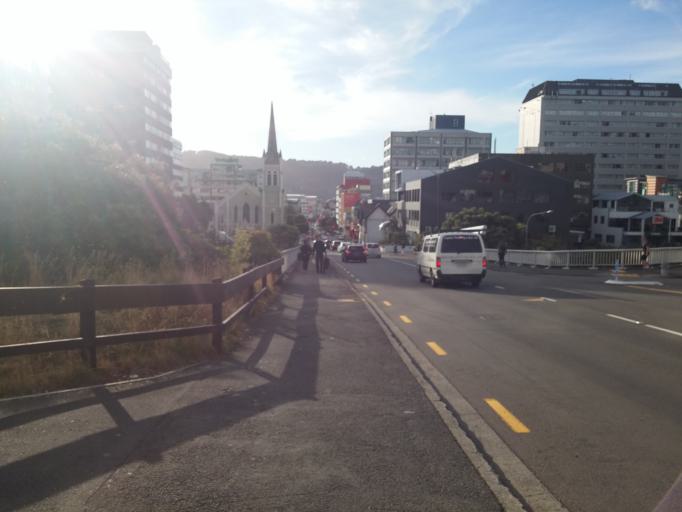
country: NZ
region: Wellington
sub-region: Wellington City
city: Wellington
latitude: -41.2918
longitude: 174.7714
